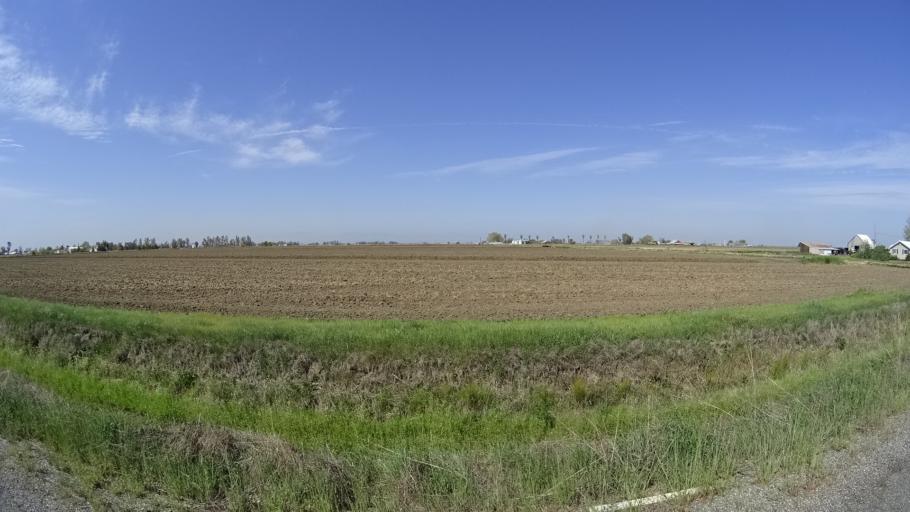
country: US
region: California
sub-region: Glenn County
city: Hamilton City
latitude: 39.5900
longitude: -122.0276
